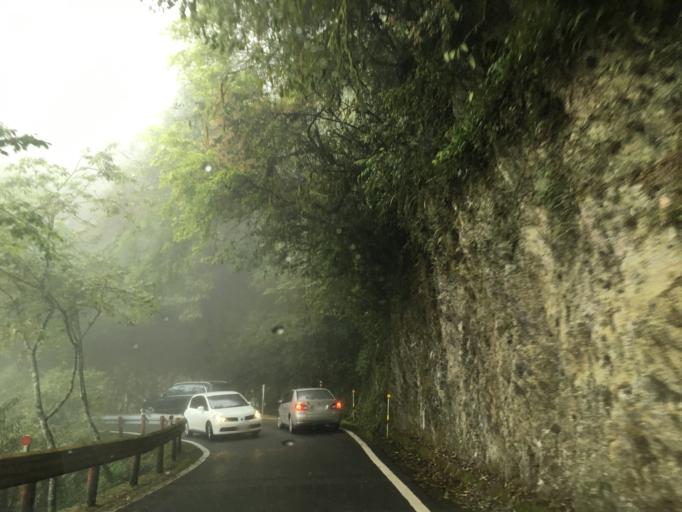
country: TW
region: Taiwan
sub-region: Hualien
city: Hualian
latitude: 24.1868
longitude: 121.4143
